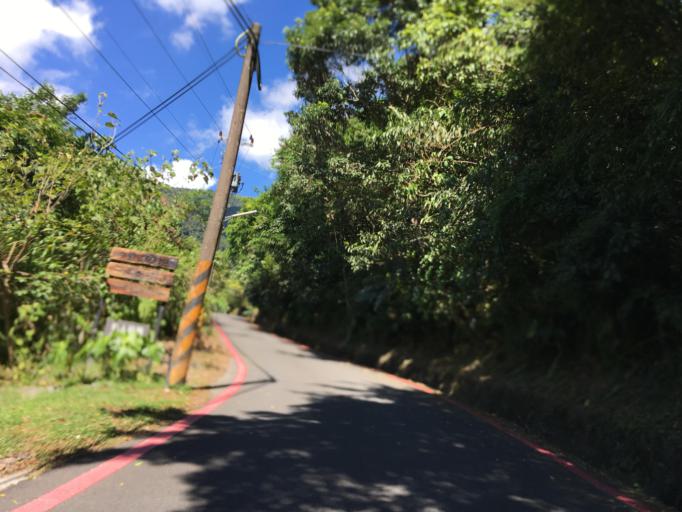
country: TW
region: Taiwan
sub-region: Yilan
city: Yilan
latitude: 24.7860
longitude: 121.6829
